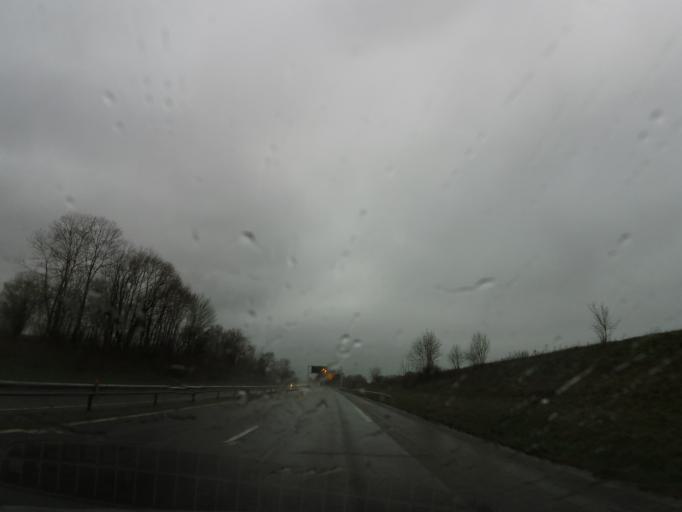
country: FR
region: Rhone-Alpes
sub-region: Departement de l'Ain
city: Bage-la-Ville
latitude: 46.2870
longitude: 4.9396
